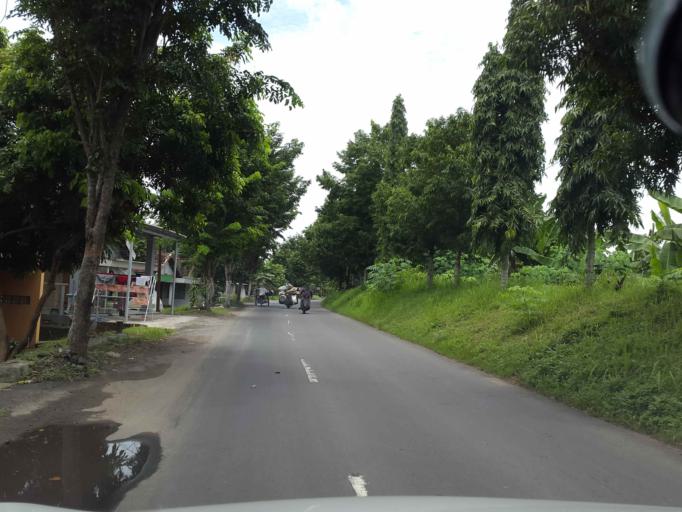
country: ID
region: East Java
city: Mojokerto
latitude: -7.4579
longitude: 112.4198
